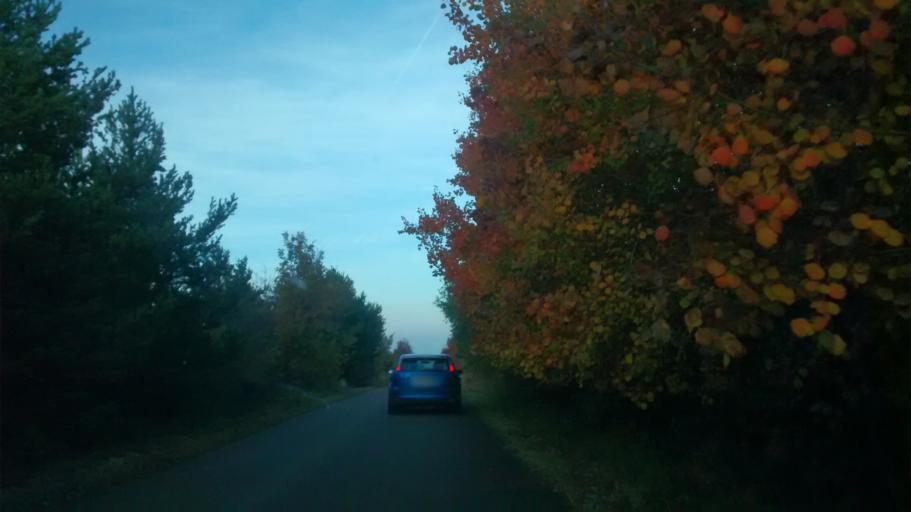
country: ES
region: Aragon
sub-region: Provincia de Zaragoza
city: Litago
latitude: 41.7902
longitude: -1.7674
